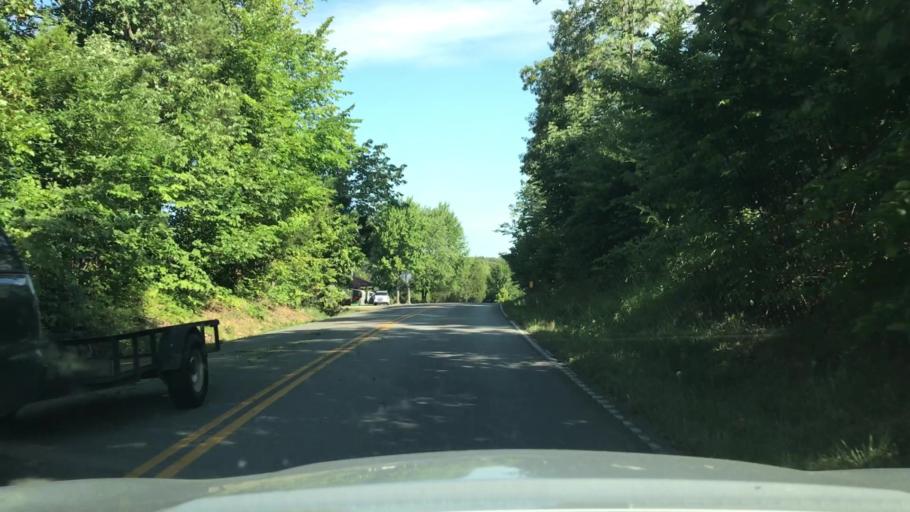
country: US
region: Kentucky
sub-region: Muhlenberg County
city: Greenville
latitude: 37.1322
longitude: -87.1413
